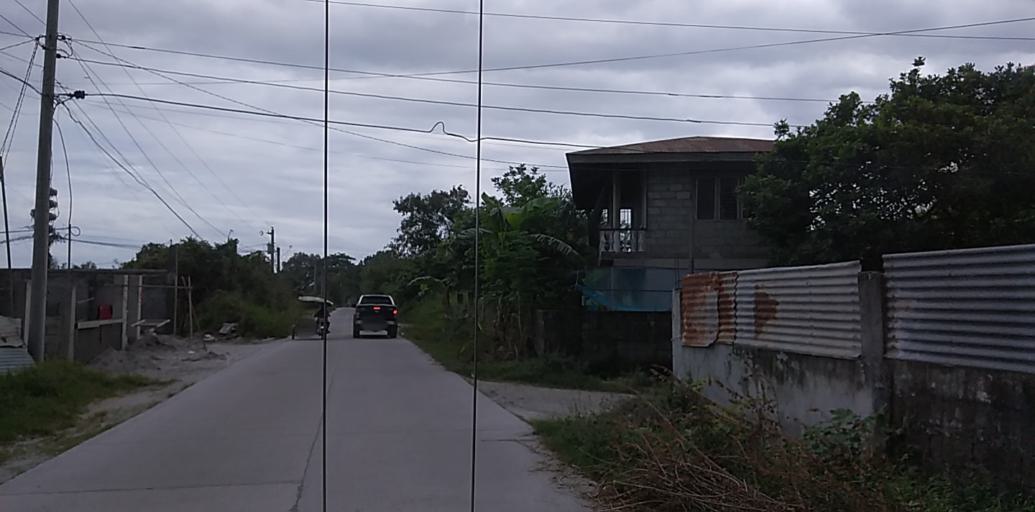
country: PH
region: Central Luzon
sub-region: Province of Pampanga
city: Porac
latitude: 15.0604
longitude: 120.5534
